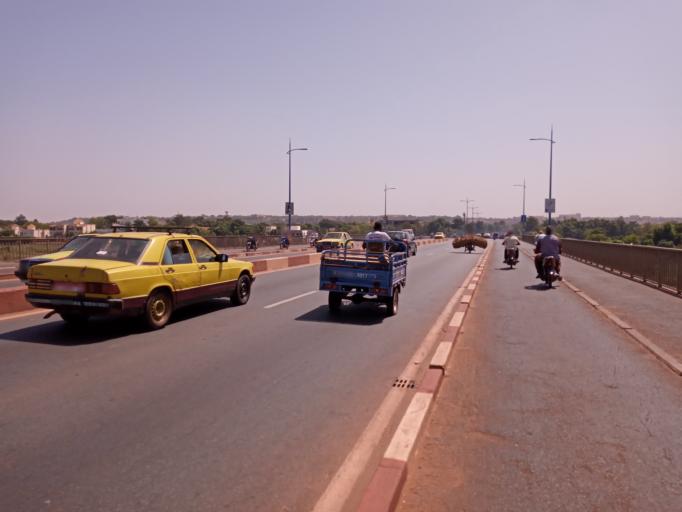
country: ML
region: Bamako
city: Bamako
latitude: 12.6217
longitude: -8.0035
